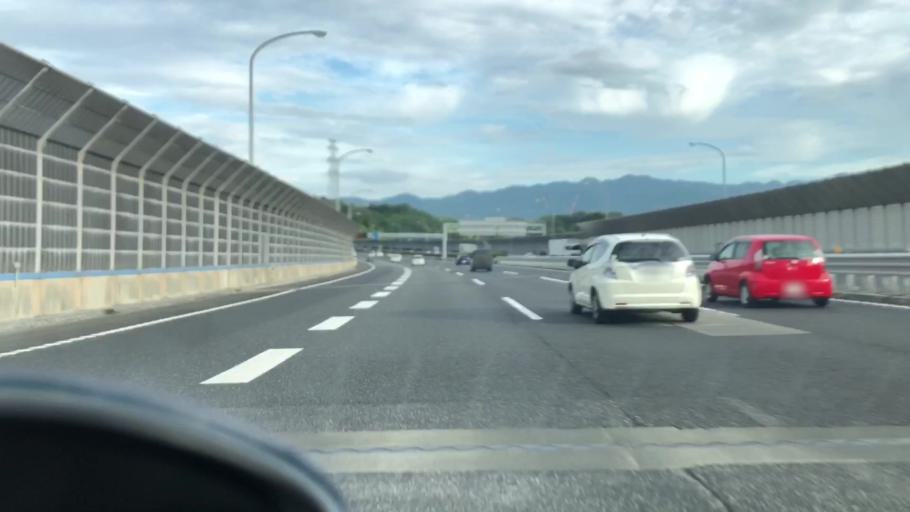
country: JP
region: Hyogo
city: Sandacho
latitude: 34.8425
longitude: 135.2275
